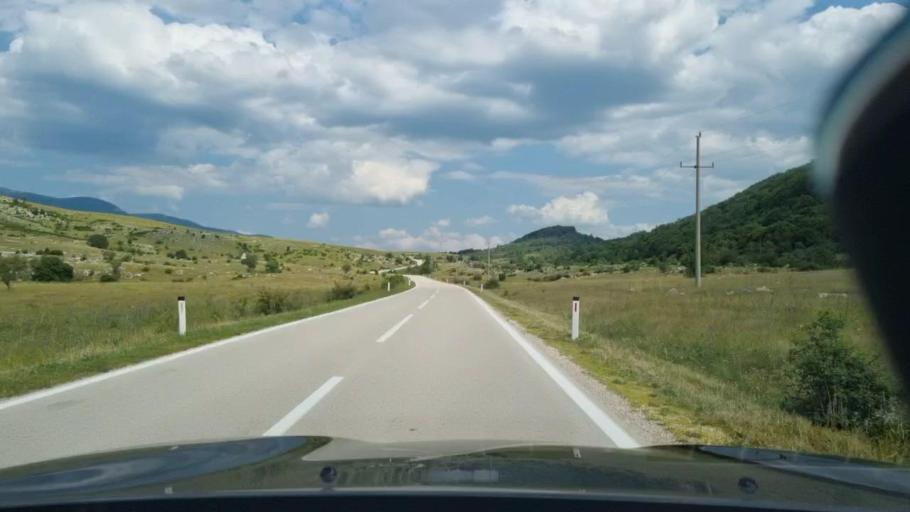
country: BA
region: Federation of Bosnia and Herzegovina
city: Bosansko Grahovo
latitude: 44.1319
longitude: 16.4865
